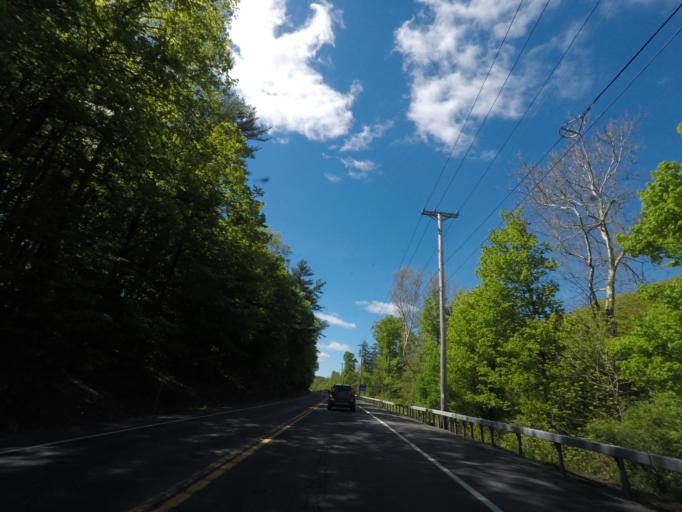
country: US
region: New York
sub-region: Ulster County
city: Glasco
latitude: 42.0310
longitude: -73.9747
